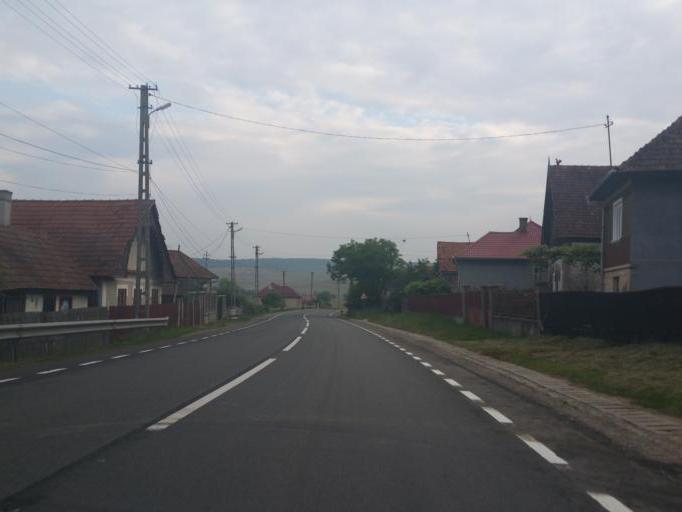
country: RO
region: Cluj
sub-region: Comuna Sanpaul
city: Sanpaul
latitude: 46.9010
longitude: 23.4154
